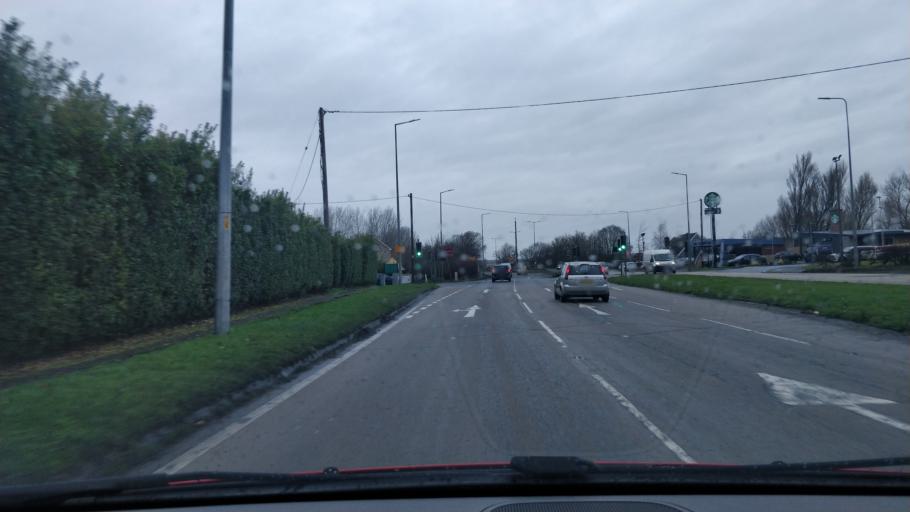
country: GB
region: England
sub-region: Sefton
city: Ince Blundell
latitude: 53.5265
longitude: -3.0316
